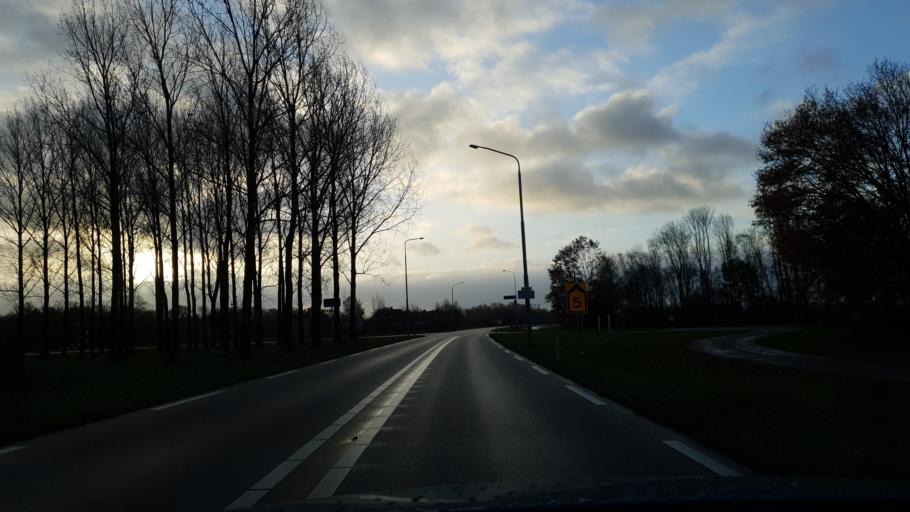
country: NL
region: Gelderland
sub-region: Gemeente Wijchen
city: Bergharen
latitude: 51.8204
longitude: 5.6898
